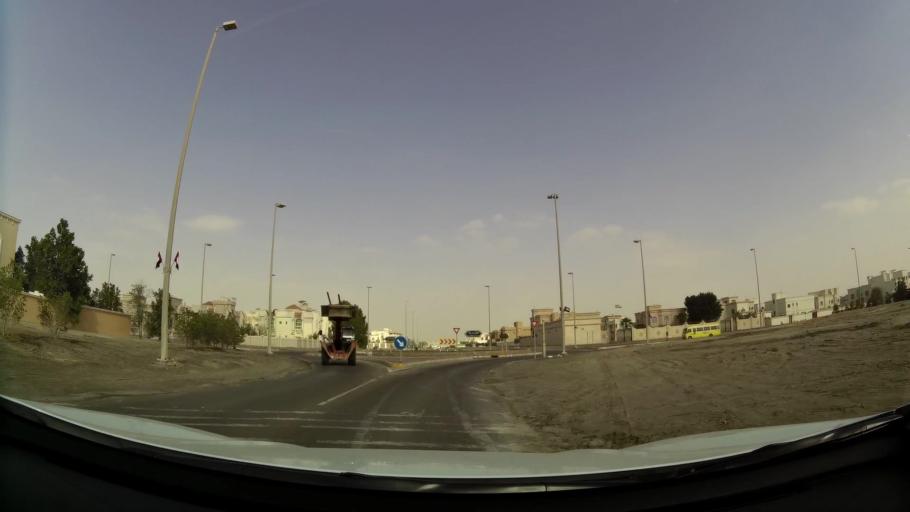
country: AE
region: Abu Dhabi
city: Abu Dhabi
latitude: 24.4153
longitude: 54.5932
